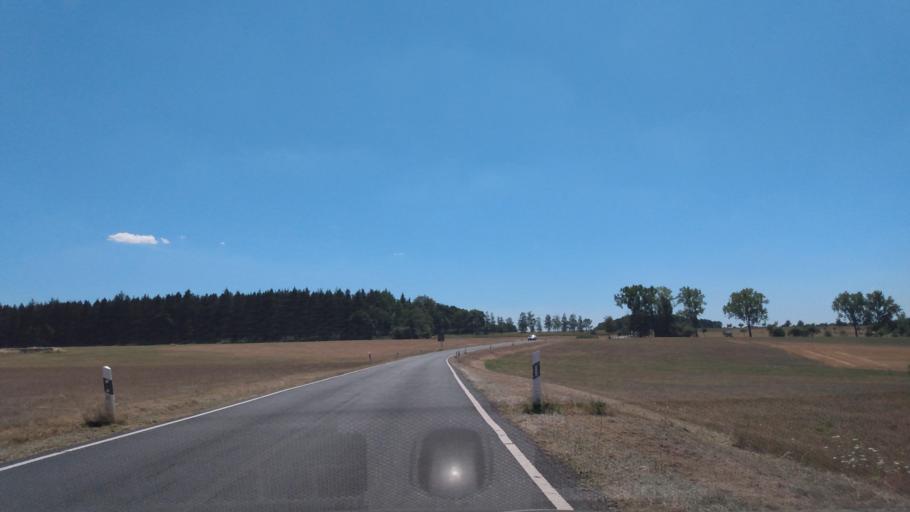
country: DE
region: Rheinland-Pfalz
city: Gransdorf
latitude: 50.0201
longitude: 6.6984
